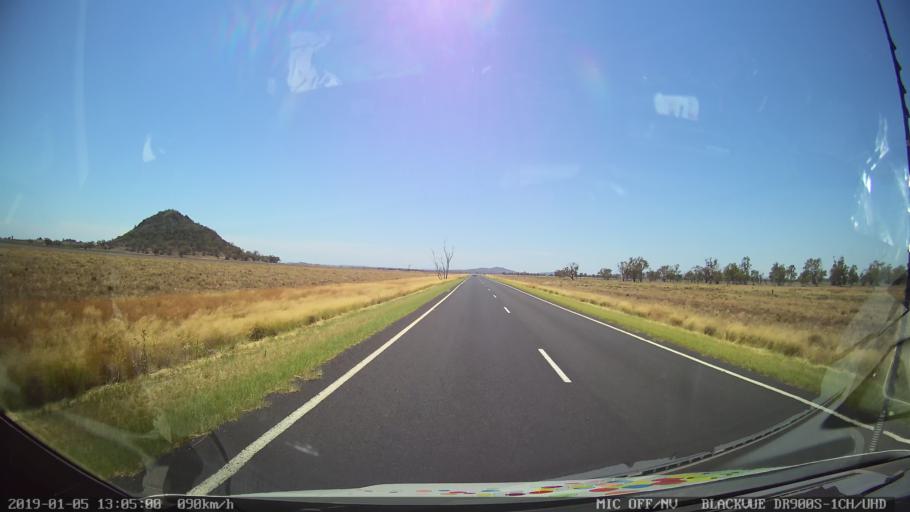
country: AU
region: New South Wales
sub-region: Gunnedah
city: Gunnedah
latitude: -31.0988
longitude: 149.8473
